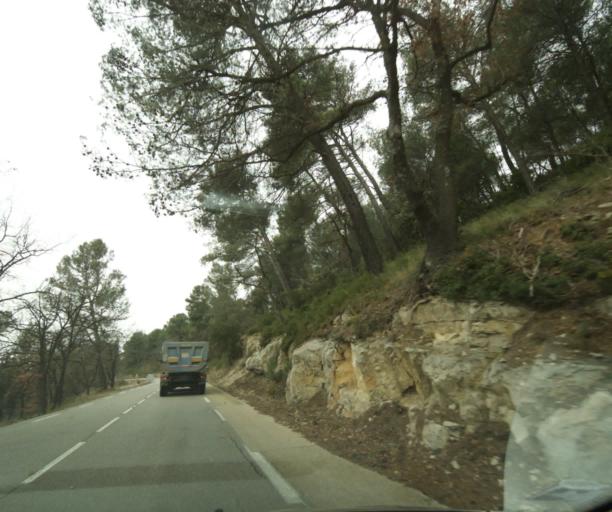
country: FR
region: Provence-Alpes-Cote d'Azur
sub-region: Departement des Bouches-du-Rhone
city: Peynier
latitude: 43.4286
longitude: 5.6212
